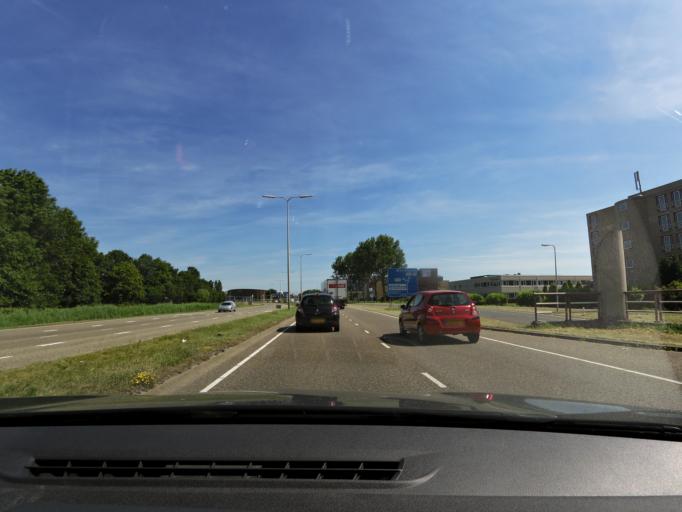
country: NL
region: South Holland
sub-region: Gemeente Spijkenisse
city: Spijkenisse
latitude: 51.8531
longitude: 4.3063
